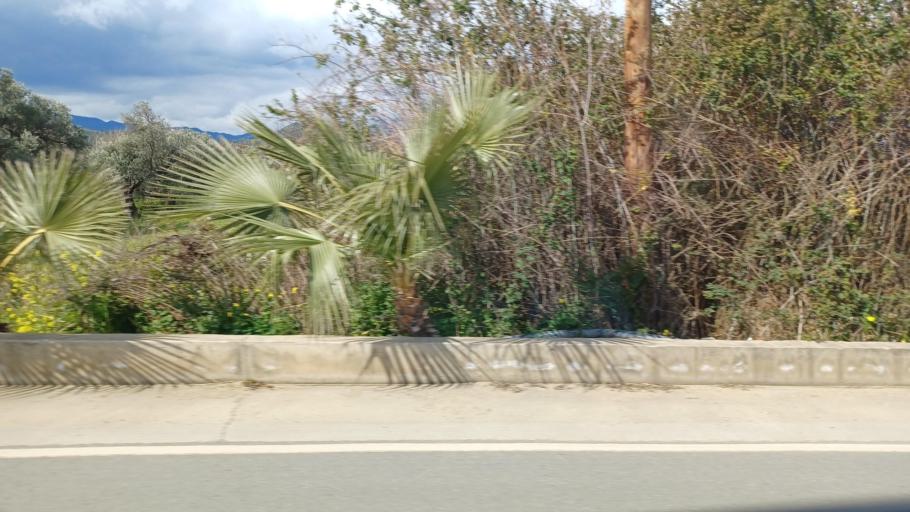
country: CY
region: Lefkosia
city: Lefka
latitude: 35.0871
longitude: 32.8892
